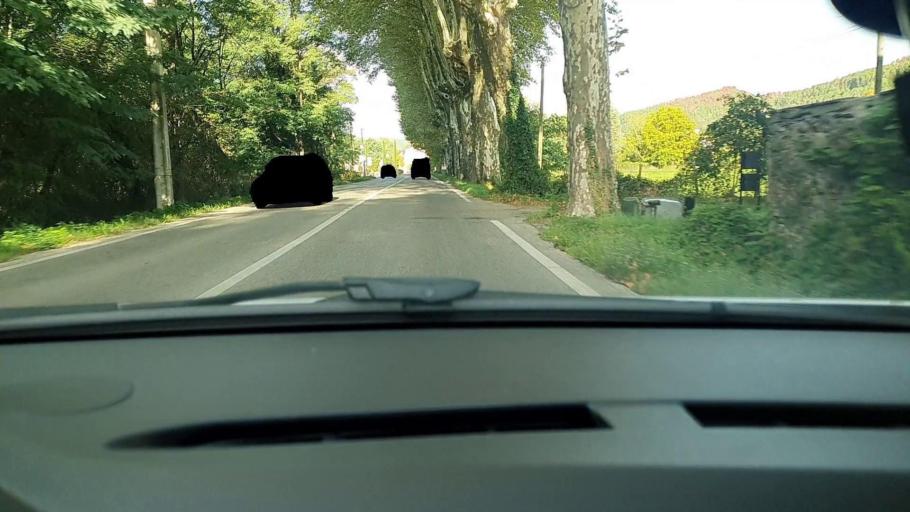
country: FR
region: Languedoc-Roussillon
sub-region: Departement du Gard
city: Besseges
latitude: 44.2857
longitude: 4.1123
